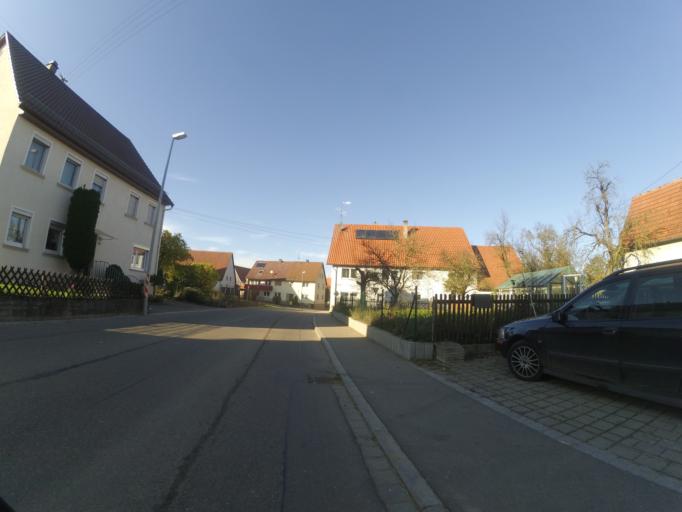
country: DE
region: Baden-Wuerttemberg
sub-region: Tuebingen Region
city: Blaubeuren
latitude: 48.4359
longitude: 9.8185
